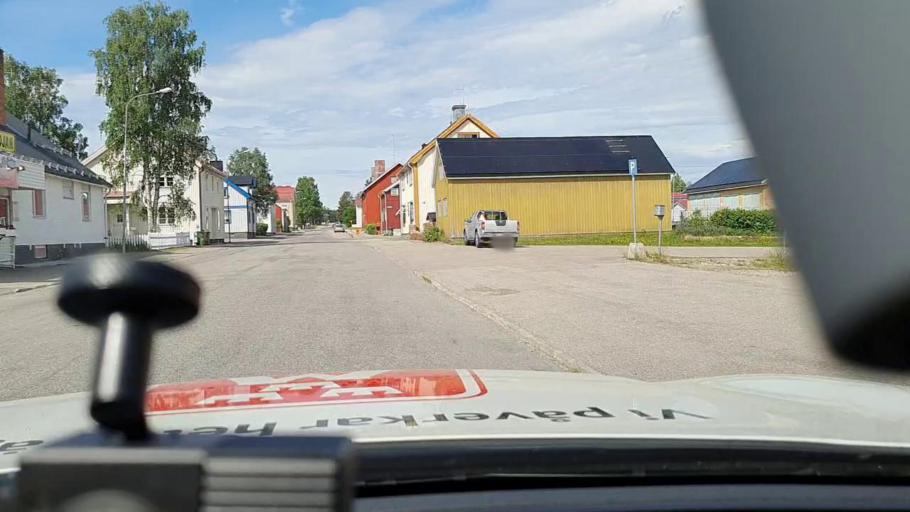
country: SE
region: Norrbotten
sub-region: Jokkmokks Kommun
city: Jokkmokk
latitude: 66.6074
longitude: 19.8287
